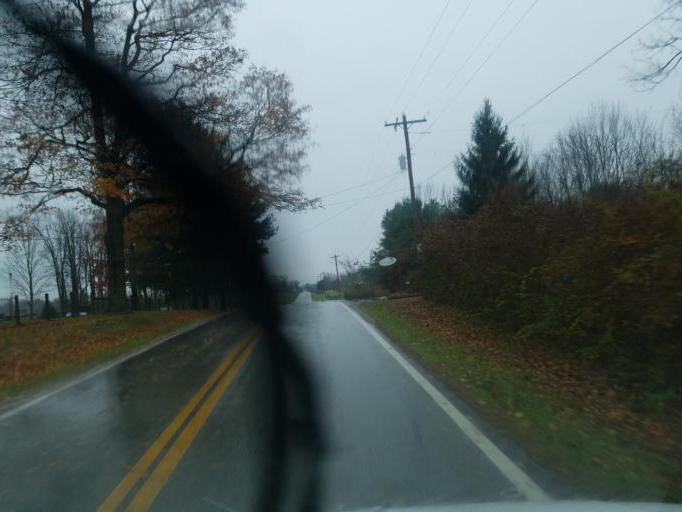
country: US
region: Ohio
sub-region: Knox County
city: Centerburg
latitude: 40.3380
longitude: -82.7938
